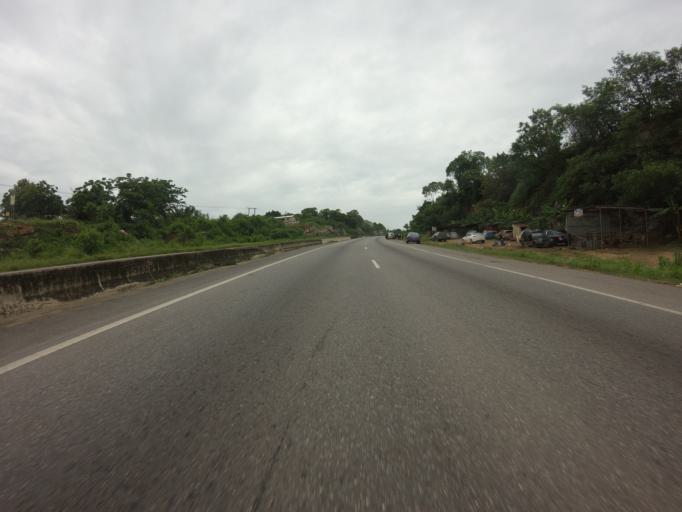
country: GH
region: Eastern
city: Nsawam
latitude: 5.8072
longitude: -0.3656
